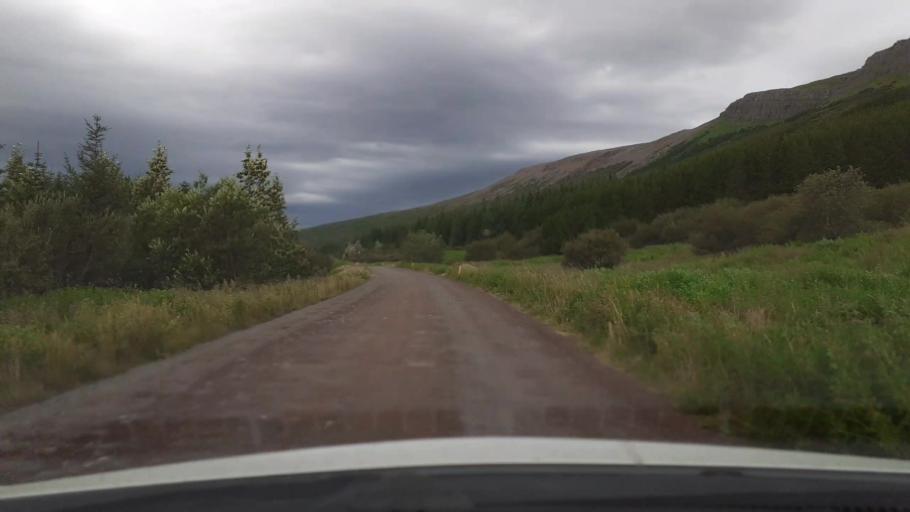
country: IS
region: West
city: Borgarnes
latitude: 64.5356
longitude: -21.5215
